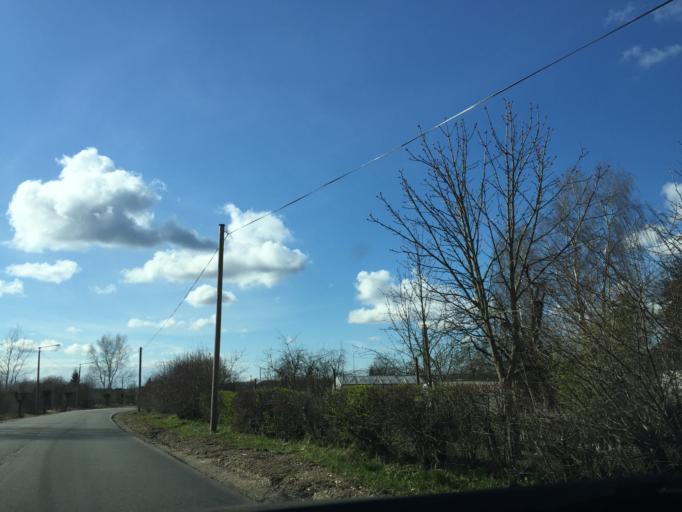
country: LV
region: Kekava
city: Kekava
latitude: 56.8219
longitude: 24.2128
